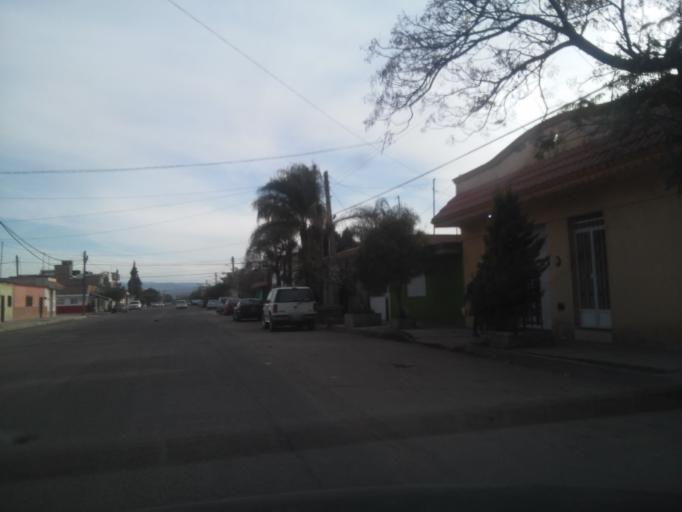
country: MX
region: Durango
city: Victoria de Durango
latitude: 24.0228
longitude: -104.6350
